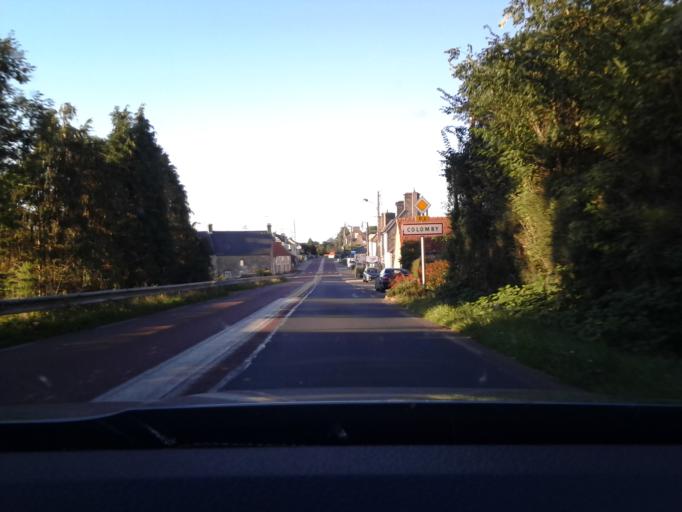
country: FR
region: Lower Normandy
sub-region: Departement de la Manche
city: Valognes
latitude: 49.4544
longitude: -1.4933
